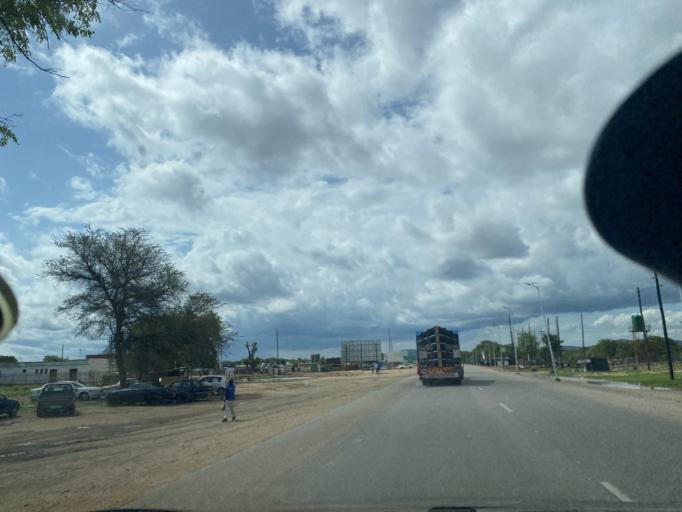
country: ZM
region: Lusaka
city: Kafue
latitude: -15.8511
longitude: 28.2501
